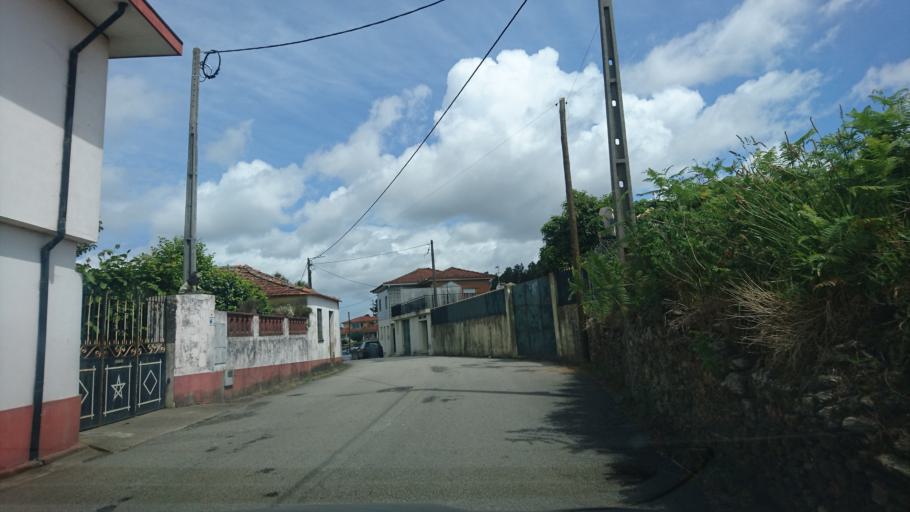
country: PT
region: Aveiro
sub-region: Santa Maria da Feira
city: Rio Meao
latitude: 40.9213
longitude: -8.5822
